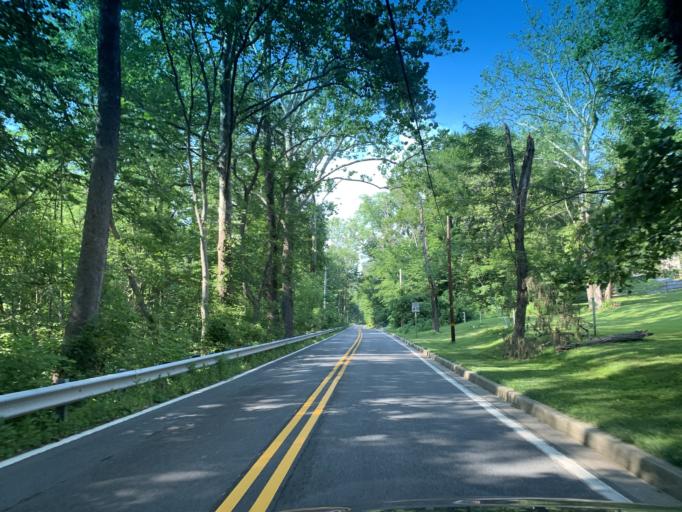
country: US
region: Maryland
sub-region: Frederick County
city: Urbana
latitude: 39.2708
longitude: -77.3396
